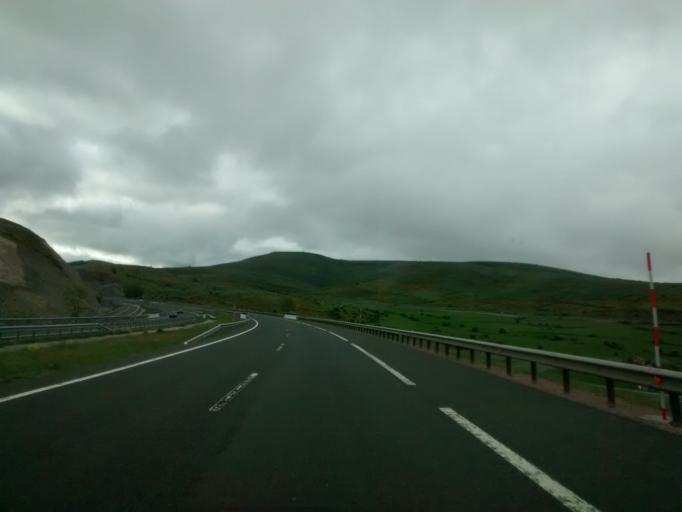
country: ES
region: Cantabria
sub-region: Provincia de Cantabria
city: Villaescusa
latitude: 42.9421
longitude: -4.1269
